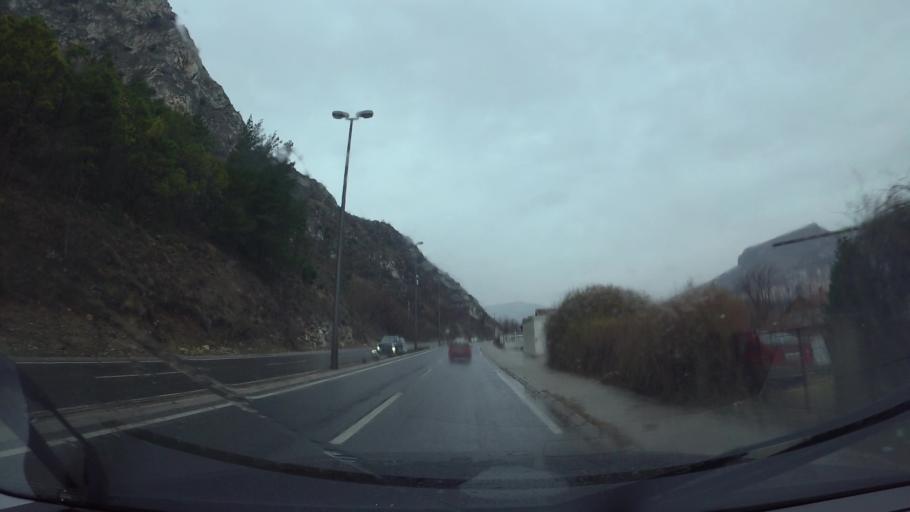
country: BA
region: Federation of Bosnia and Herzegovina
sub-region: Hercegovacko-Bosanski Kanton
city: Mostar
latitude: 43.3288
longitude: 17.8157
